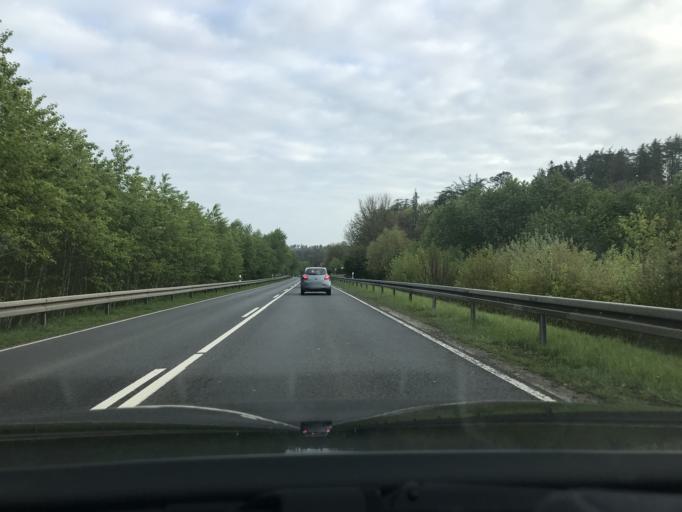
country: DE
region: Thuringia
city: Kallmerode
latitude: 51.3594
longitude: 10.3044
